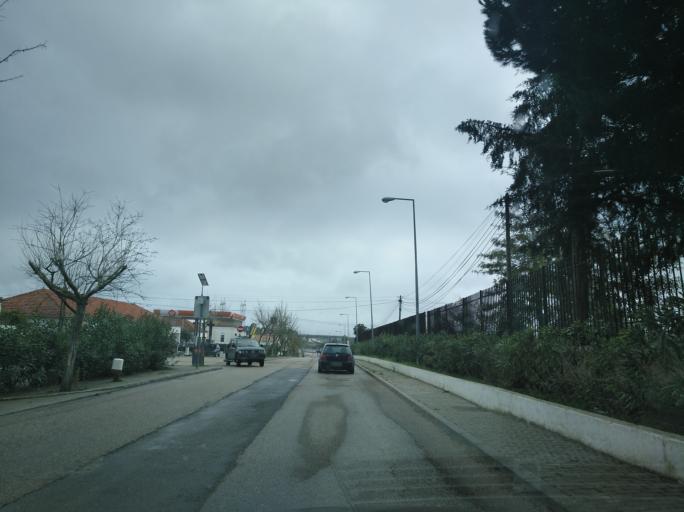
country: PT
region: Setubal
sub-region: Grandola
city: Grandola
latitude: 38.1711
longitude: -8.5576
